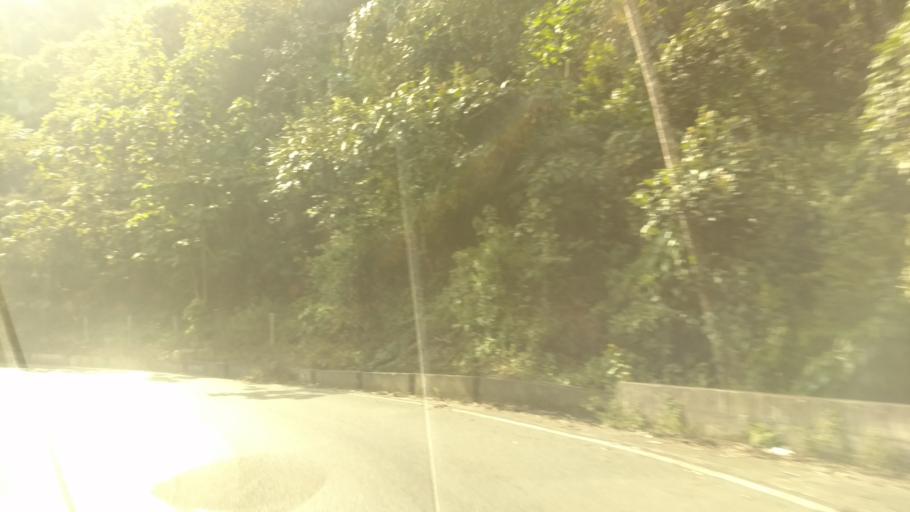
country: CO
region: Caldas
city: Neira
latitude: 5.1468
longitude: -75.5071
